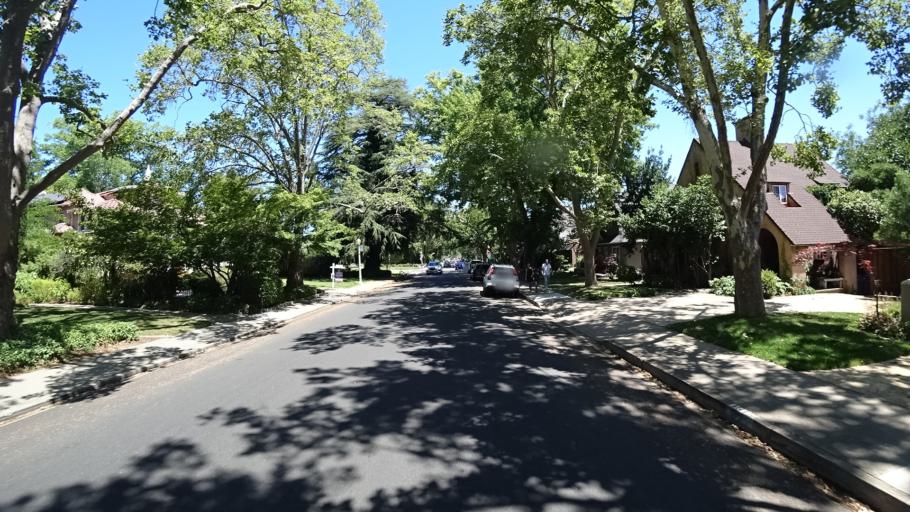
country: US
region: California
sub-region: Sacramento County
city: Sacramento
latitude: 38.5666
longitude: -121.4560
